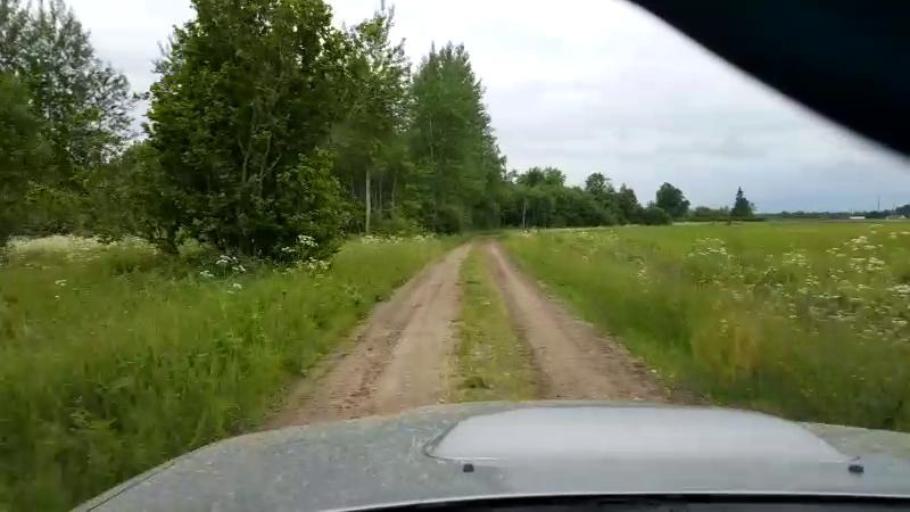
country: EE
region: Paernumaa
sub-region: Tootsi vald
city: Tootsi
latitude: 58.5925
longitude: 24.6630
